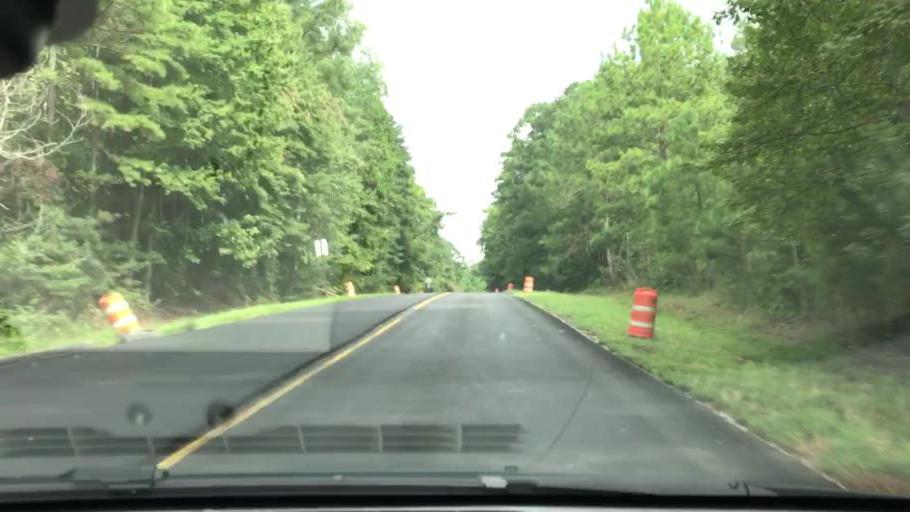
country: US
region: Georgia
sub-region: Clay County
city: Fort Gaines
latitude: 31.5954
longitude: -85.0412
